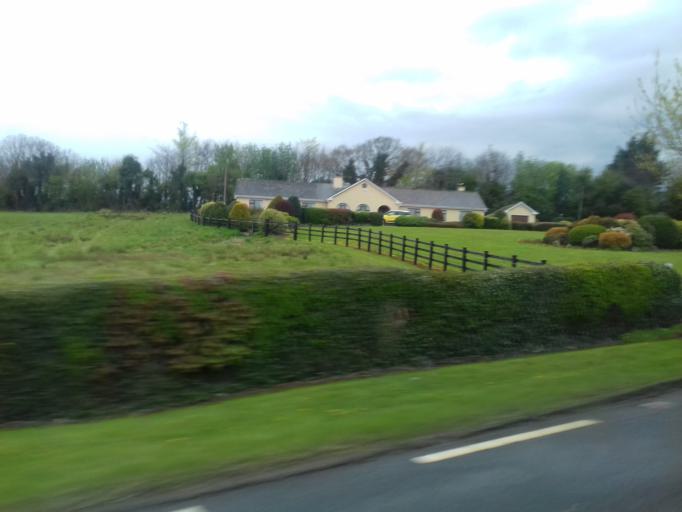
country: IE
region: Ulster
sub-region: An Cabhan
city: Ballyconnell
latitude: 54.0974
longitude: -7.5539
